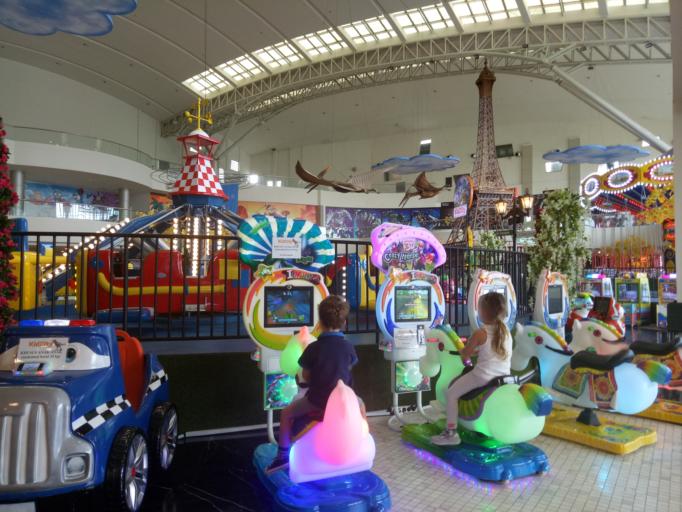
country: ID
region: East Java
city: Jagirsidosermo
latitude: -7.2857
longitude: 112.6811
